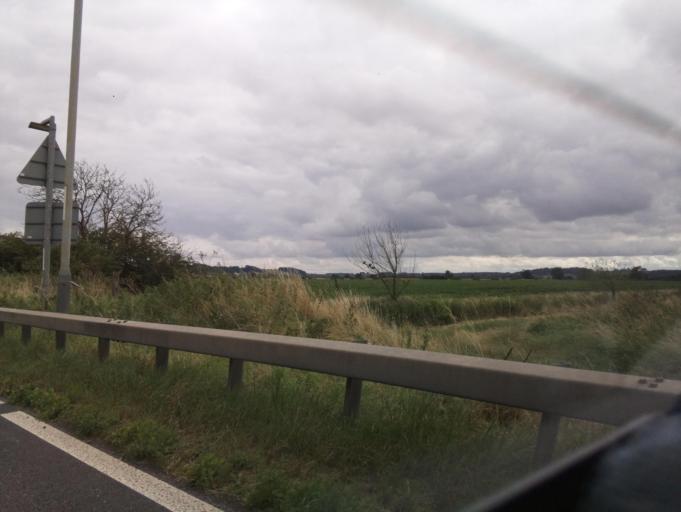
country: GB
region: England
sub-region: Lincolnshire
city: Barrowby
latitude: 52.9297
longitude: -0.7311
